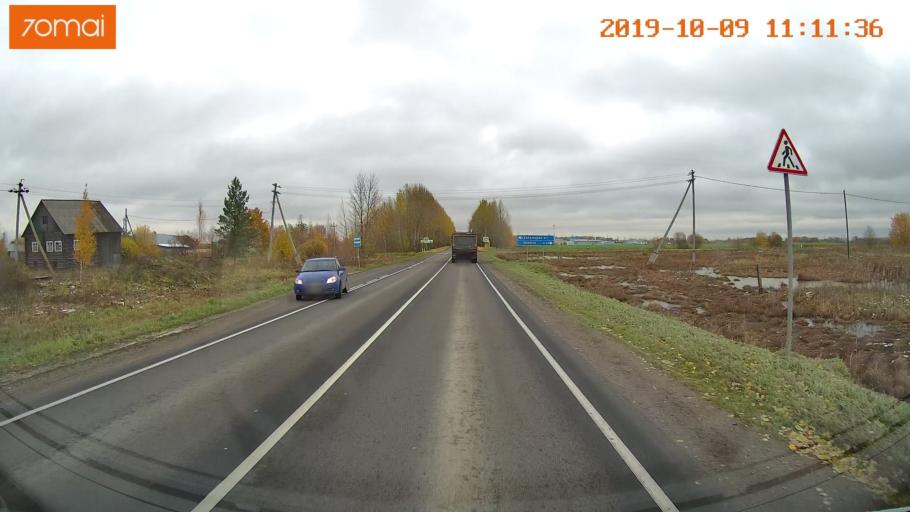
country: RU
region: Vologda
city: Vologda
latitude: 59.1696
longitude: 39.8221
